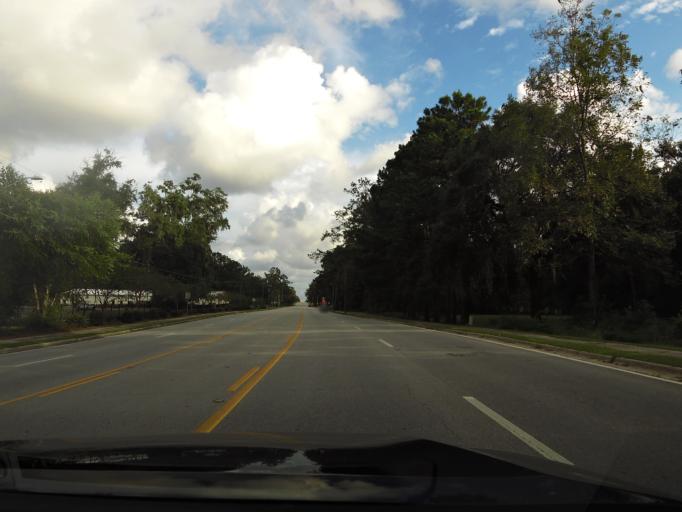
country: US
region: Georgia
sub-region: Liberty County
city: Midway
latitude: 31.7413
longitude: -81.4392
